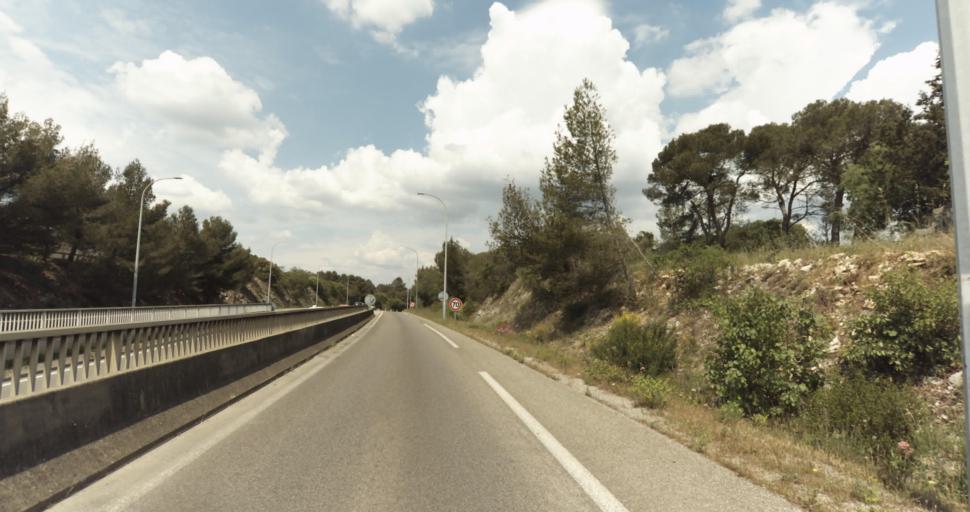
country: FR
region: Languedoc-Roussillon
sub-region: Departement du Gard
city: Nimes
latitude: 43.8417
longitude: 4.3187
